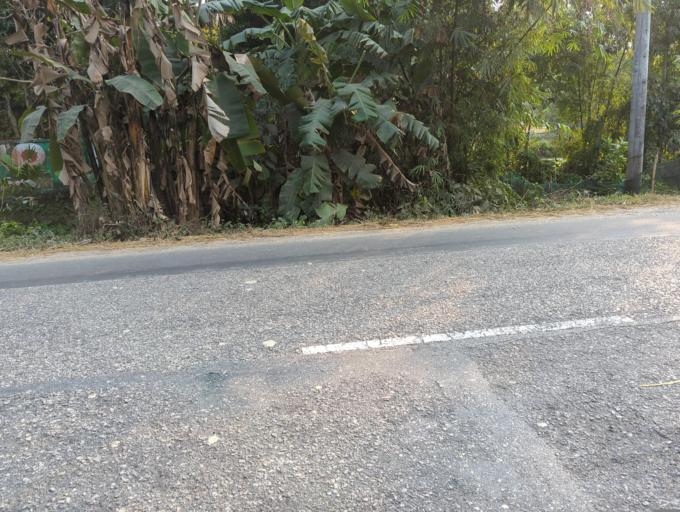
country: BD
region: Sylhet
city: Maulavi Bazar
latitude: 24.5758
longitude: 91.7175
